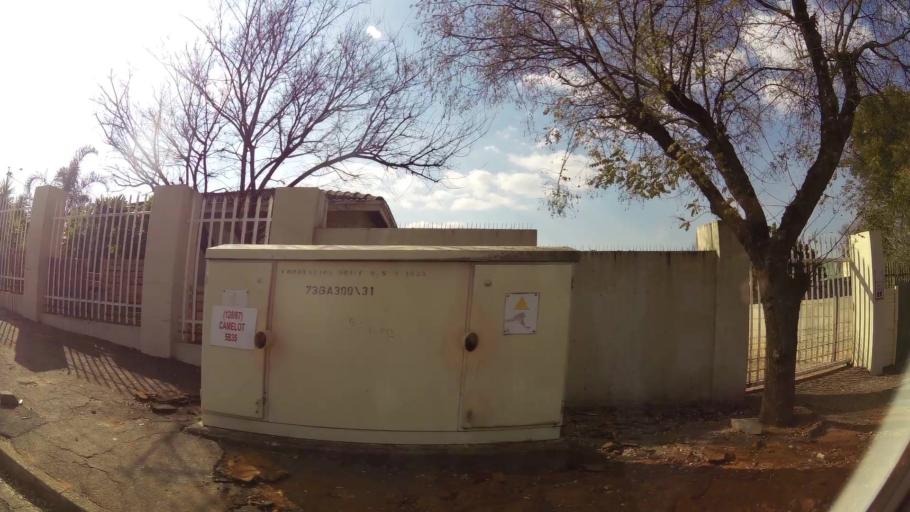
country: ZA
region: Gauteng
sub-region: Ekurhuleni Metropolitan Municipality
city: Germiston
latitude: -26.1791
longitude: 28.1732
